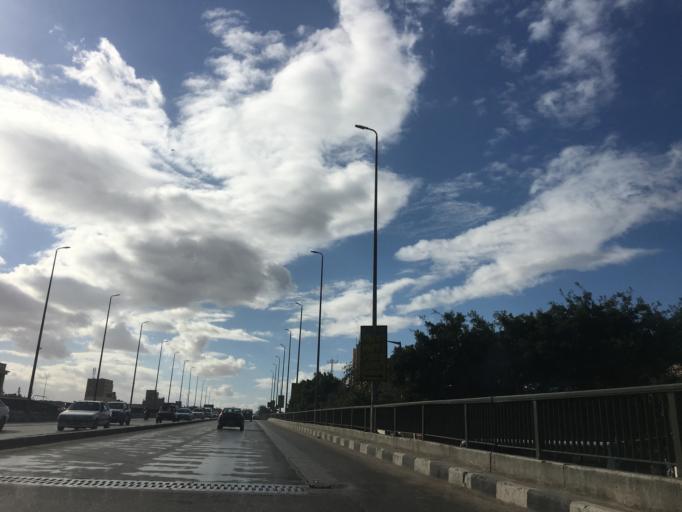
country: EG
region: Al Jizah
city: Al Jizah
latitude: 30.0279
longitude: 31.2030
